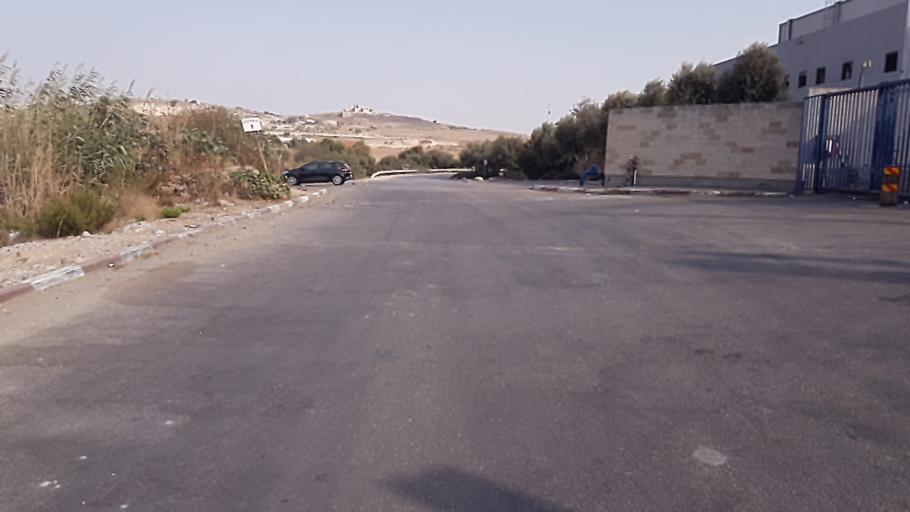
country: IL
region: Central District
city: Rosh Ha'Ayin
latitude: 32.0843
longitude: 34.9431
